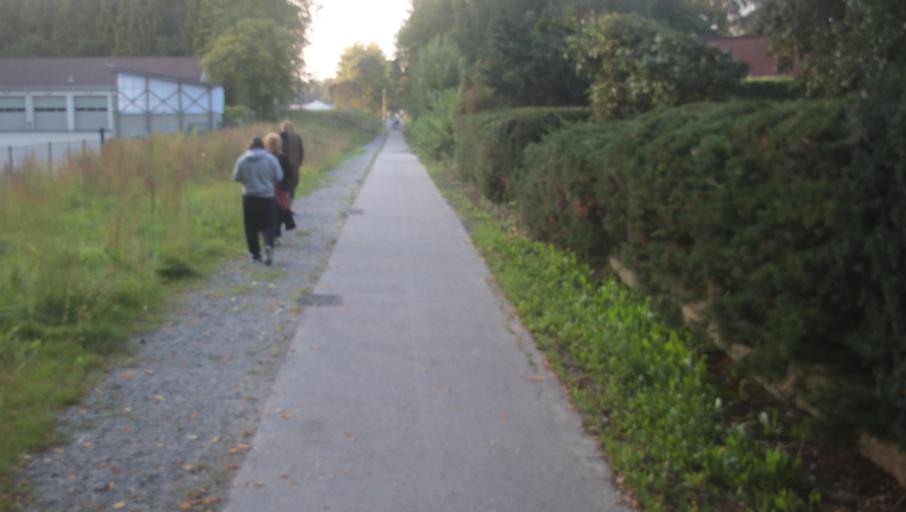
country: SE
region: Blekinge
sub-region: Karlshamns Kommun
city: Karlshamn
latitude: 56.2064
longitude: 14.8318
